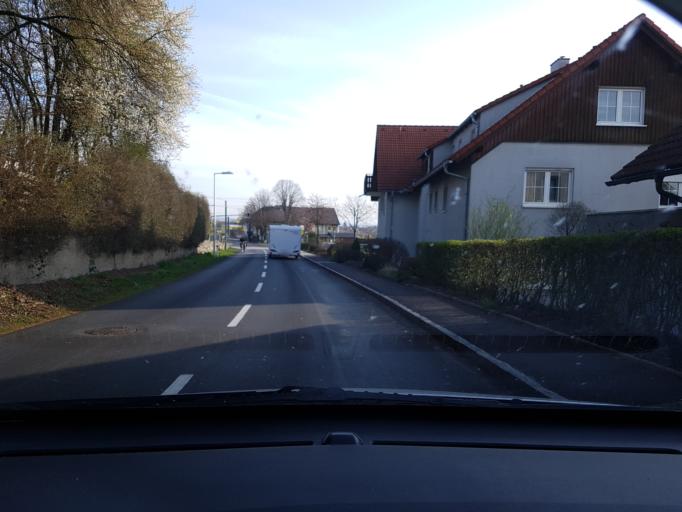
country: AT
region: Upper Austria
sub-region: Politischer Bezirk Linz-Land
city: Asten
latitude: 48.2119
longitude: 14.4003
